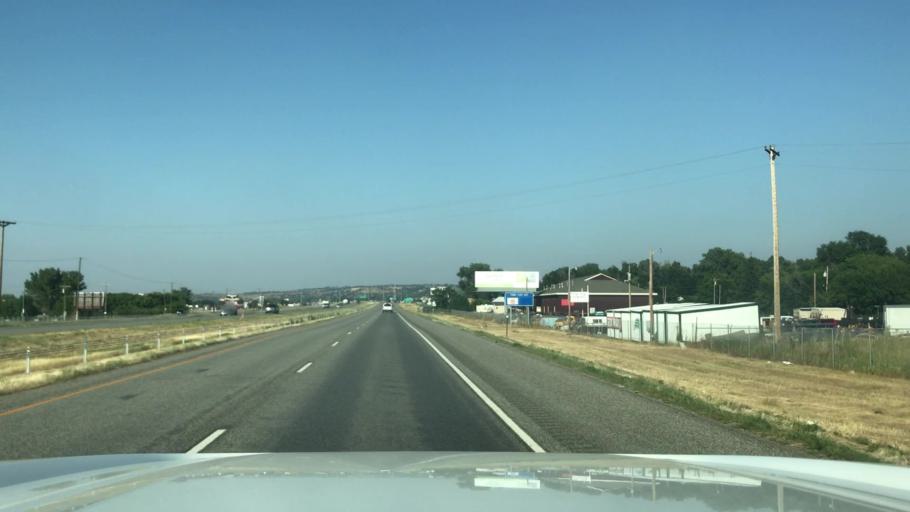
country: US
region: Montana
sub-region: Yellowstone County
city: Lockwood
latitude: 45.8083
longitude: -108.4261
